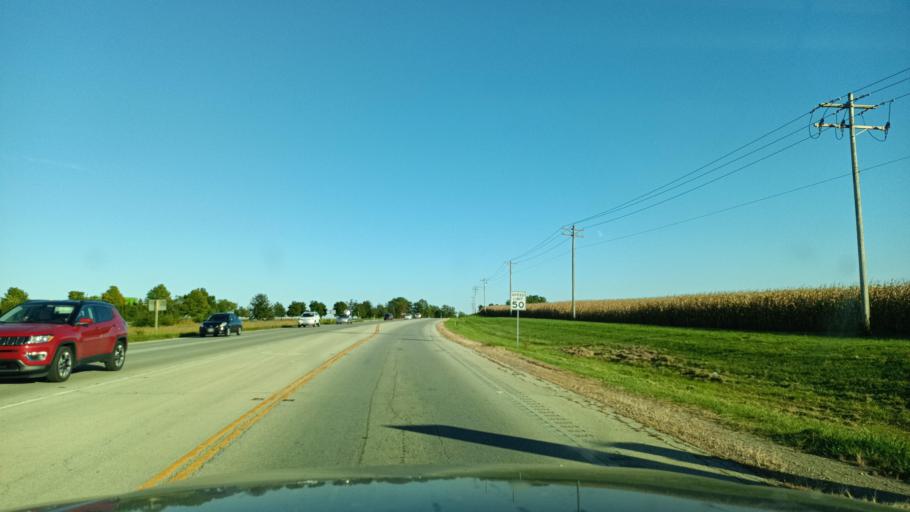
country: US
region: Illinois
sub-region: Champaign County
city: Lake of the Woods
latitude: 40.1842
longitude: -88.3648
